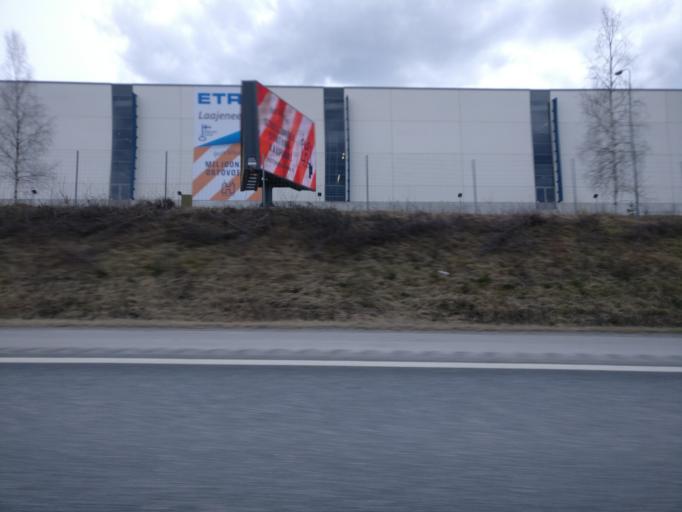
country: FI
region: Haeme
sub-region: Haemeenlinna
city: Haemeenlinna
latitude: 60.9556
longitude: 24.4884
